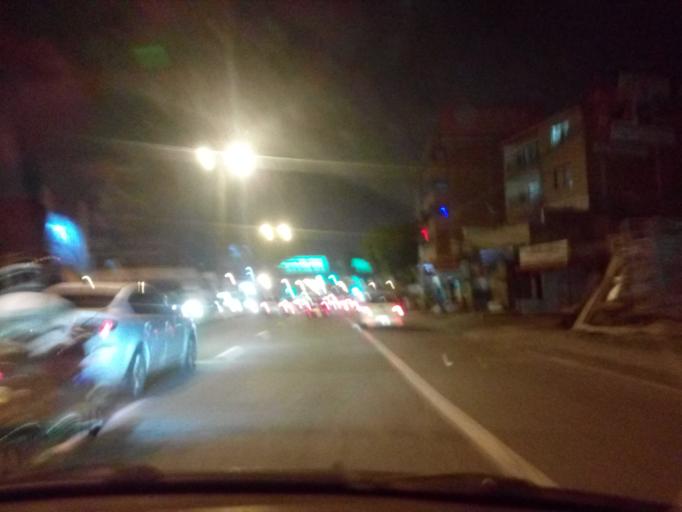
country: CO
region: Antioquia
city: Itagui
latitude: 6.1942
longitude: -75.5914
